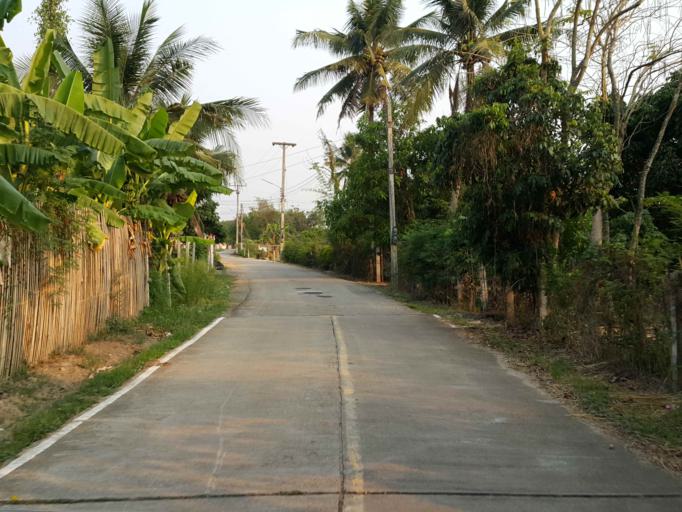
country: TH
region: Chiang Mai
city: Mae Taeng
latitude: 18.9887
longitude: 98.9811
